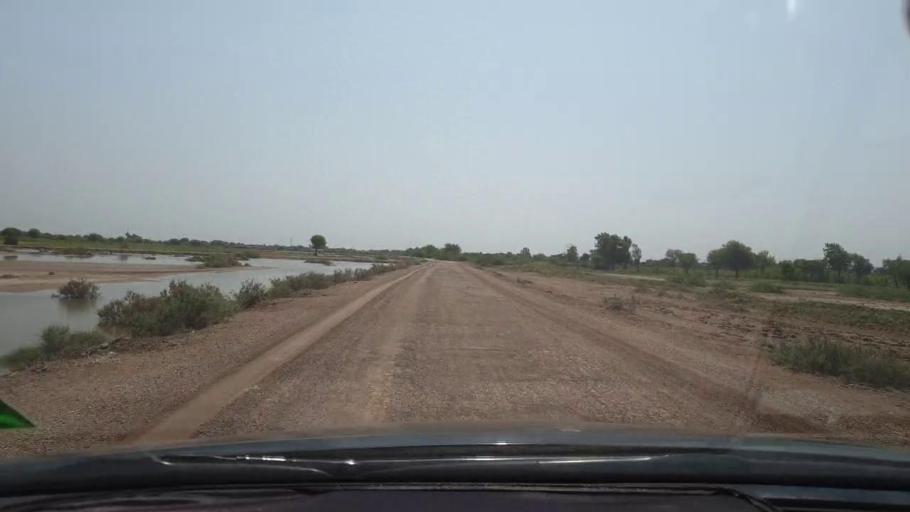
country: PK
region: Sindh
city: Tando Bago
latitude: 24.7916
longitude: 69.1693
